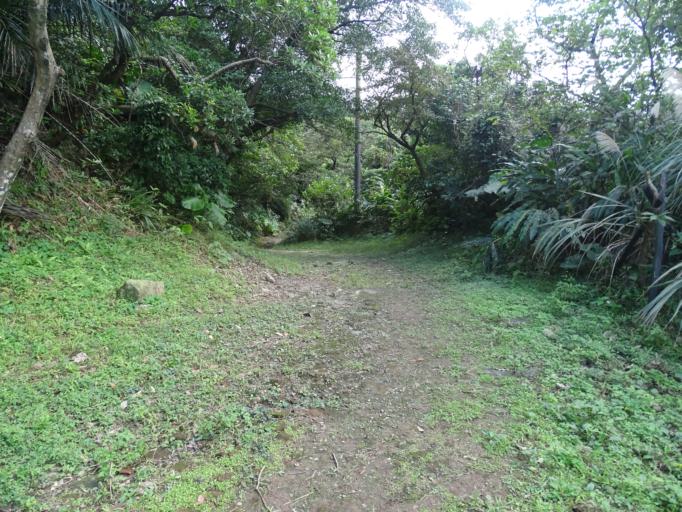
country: TW
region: Taiwan
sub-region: Keelung
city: Keelung
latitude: 25.1430
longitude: 121.7818
